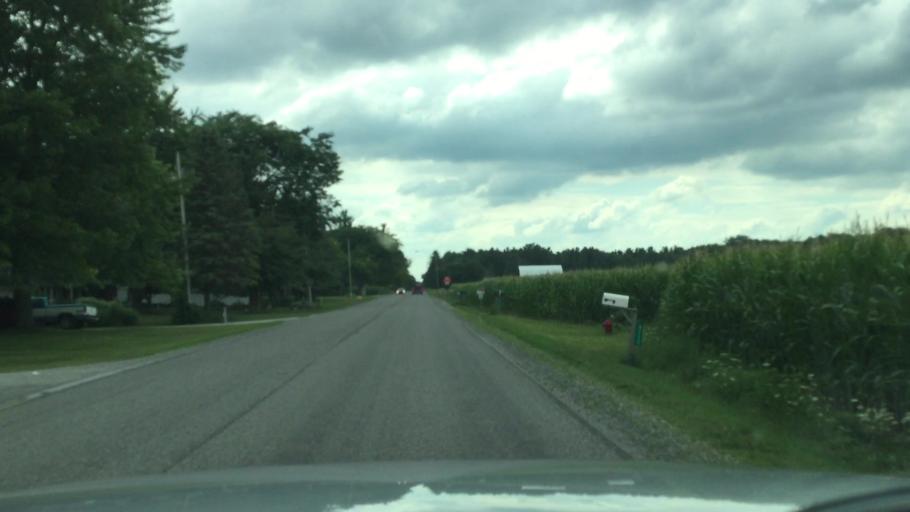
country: US
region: Michigan
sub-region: Saginaw County
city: Frankenmuth
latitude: 43.3217
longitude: -83.7735
